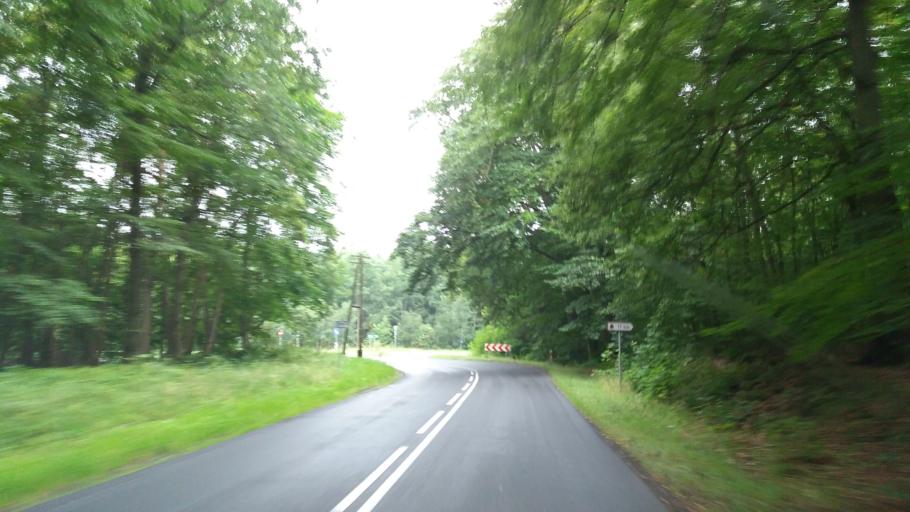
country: PL
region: West Pomeranian Voivodeship
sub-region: Powiat choszczenski
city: Pelczyce
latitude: 53.0841
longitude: 15.2822
